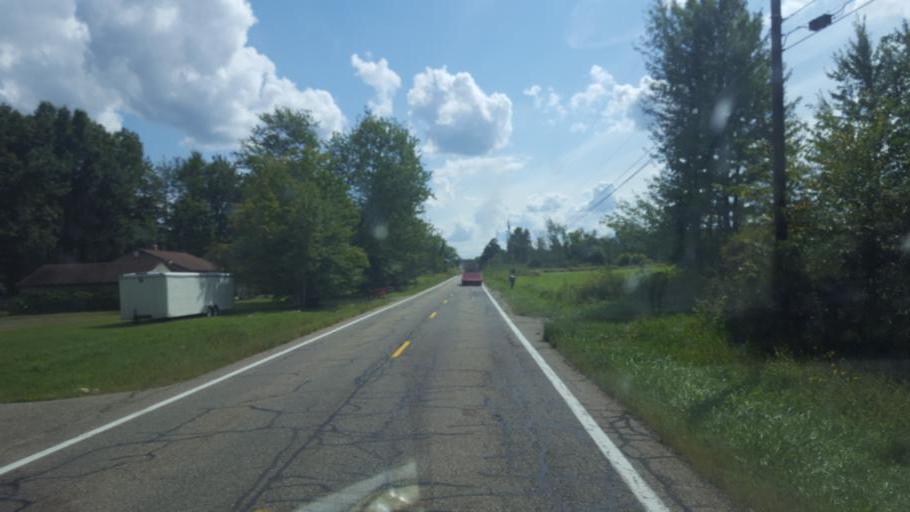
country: US
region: Ohio
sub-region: Portage County
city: Garrettsville
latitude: 41.2478
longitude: -81.1476
